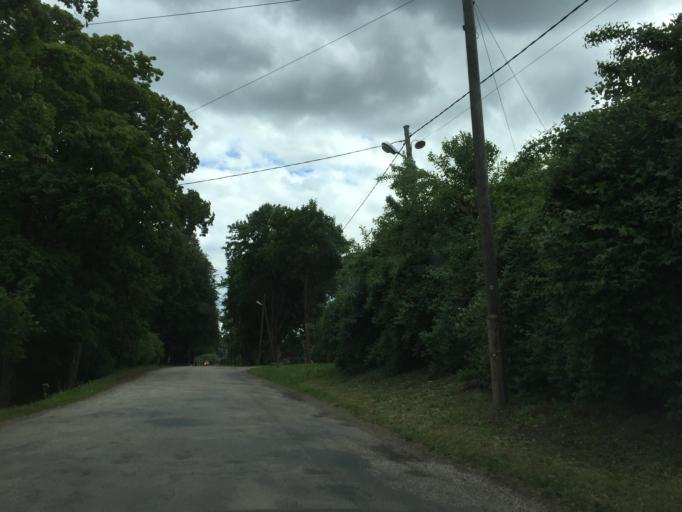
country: LV
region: Lecava
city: Iecava
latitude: 56.5925
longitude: 24.2086
